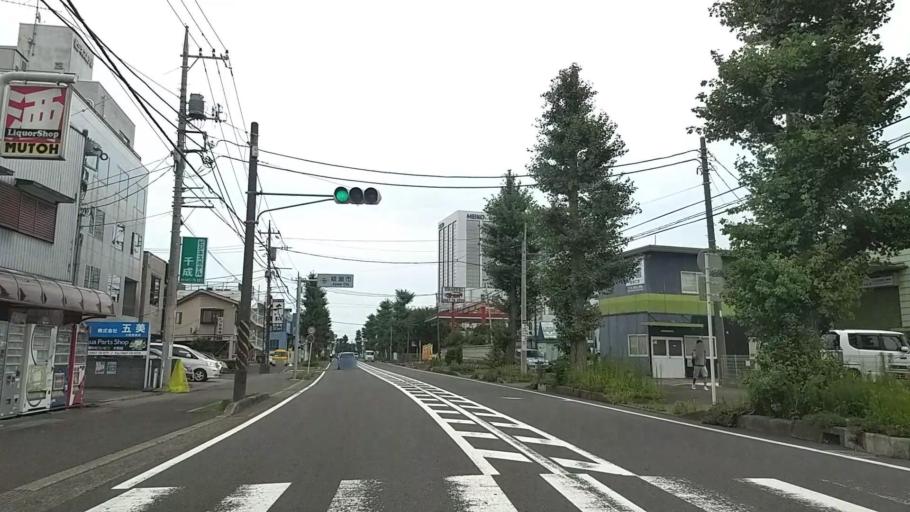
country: JP
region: Kanagawa
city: Minami-rinkan
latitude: 35.4670
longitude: 139.4299
